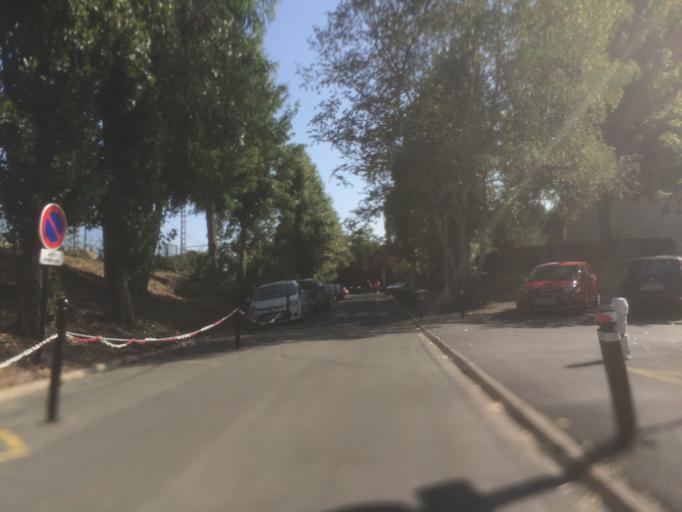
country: FR
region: Ile-de-France
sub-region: Departement de l'Essonne
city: Longjumeau
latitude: 48.6899
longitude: 2.3158
